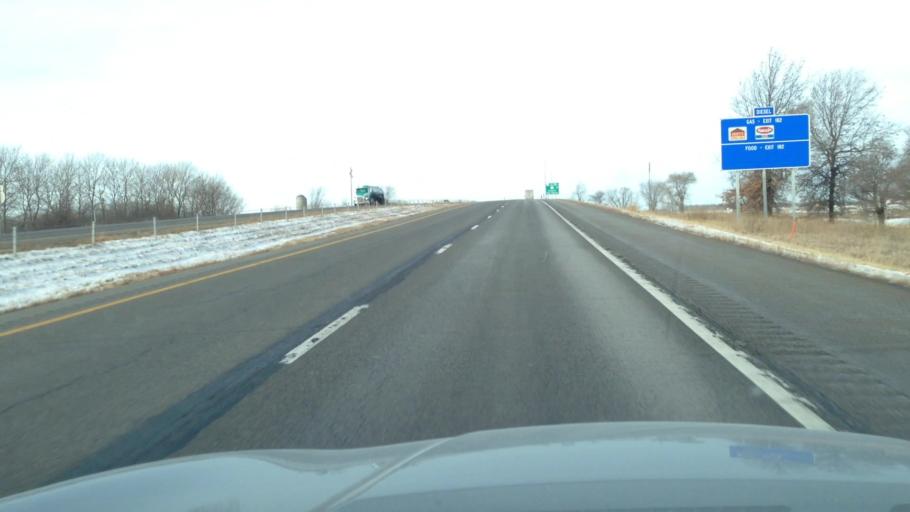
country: US
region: Iowa
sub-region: Poweshiek County
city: Grinnell
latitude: 41.6958
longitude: -92.7166
